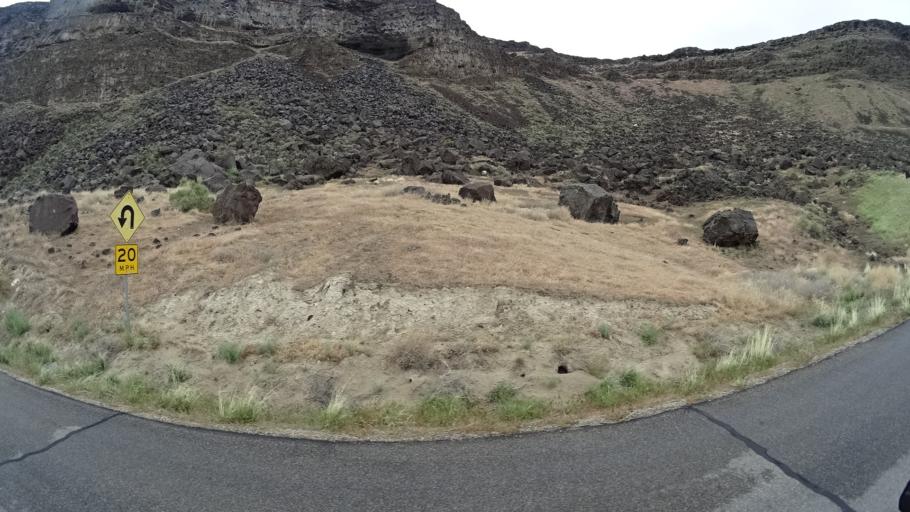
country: US
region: Idaho
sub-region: Owyhee County
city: Murphy
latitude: 43.2490
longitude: -116.3759
